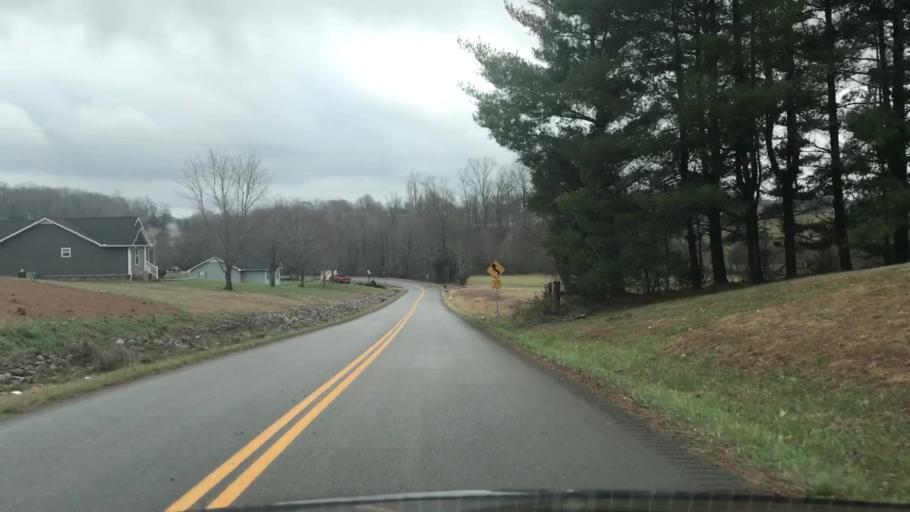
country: US
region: Kentucky
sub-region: Monroe County
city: Tompkinsville
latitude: 36.7213
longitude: -85.7087
